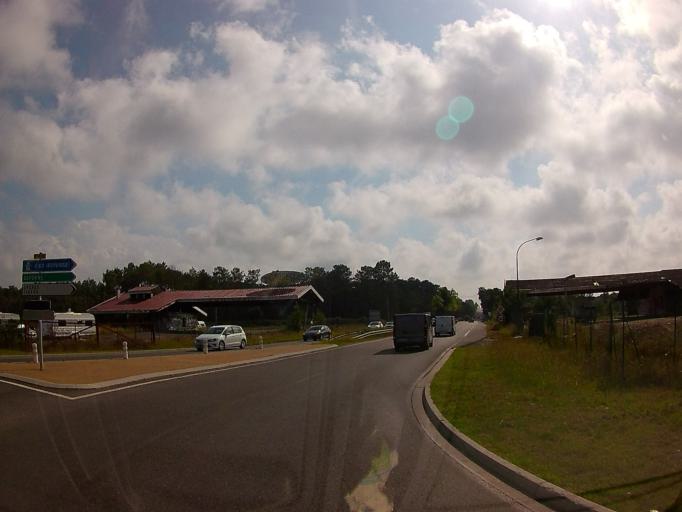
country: FR
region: Aquitaine
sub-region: Departement des Landes
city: Ondres
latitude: 43.5781
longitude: -1.4356
